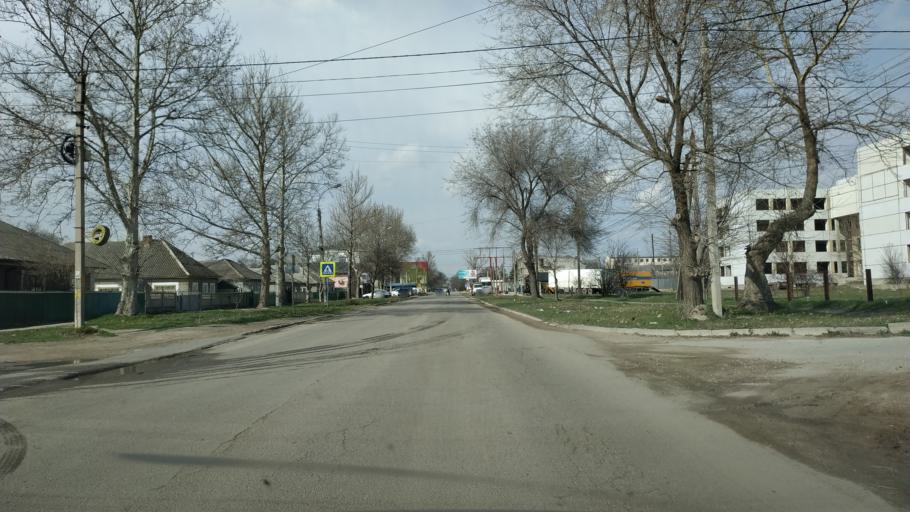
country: MD
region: Gagauzia
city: Vulcanesti
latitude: 45.6802
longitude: 28.4090
